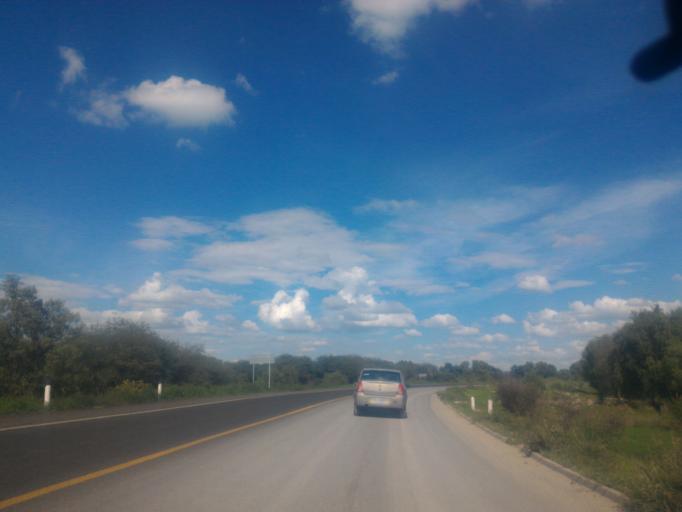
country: MX
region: Guanajuato
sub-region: Purisima del Rincon
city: Monte Grande
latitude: 21.0150
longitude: -101.8866
